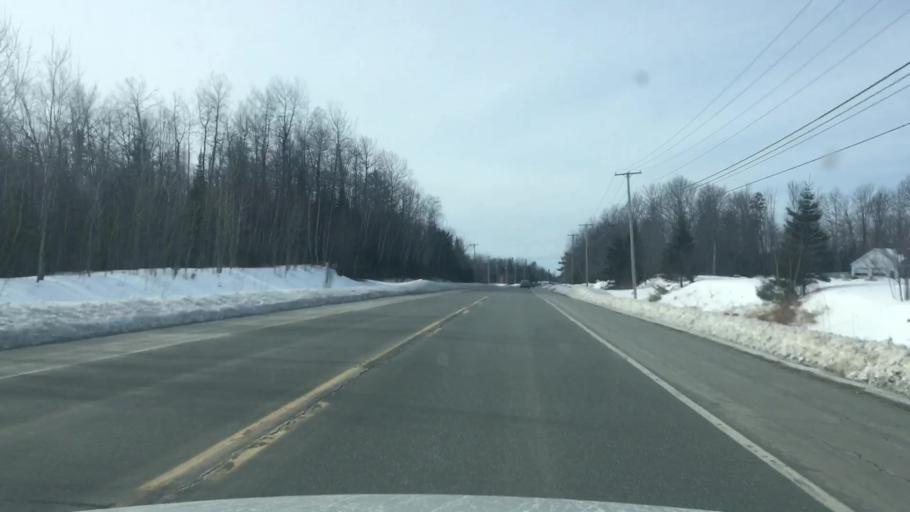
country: US
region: Maine
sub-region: Penobscot County
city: Kenduskeag
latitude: 44.9118
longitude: -68.9025
